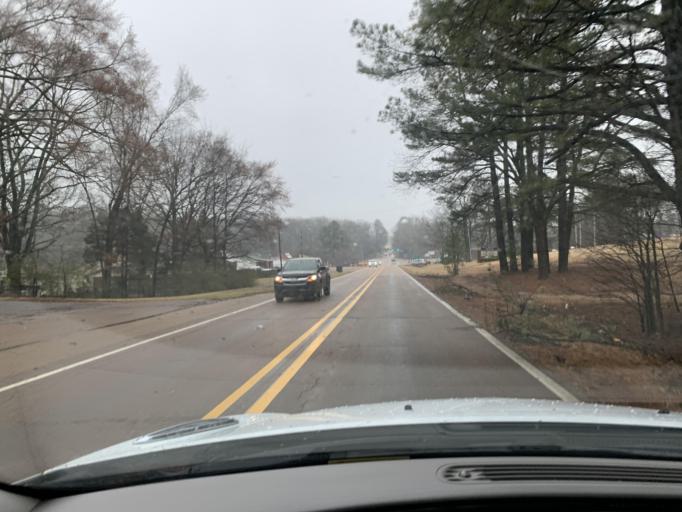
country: US
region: Mississippi
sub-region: De Soto County
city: Hernando
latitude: 34.8859
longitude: -89.9963
